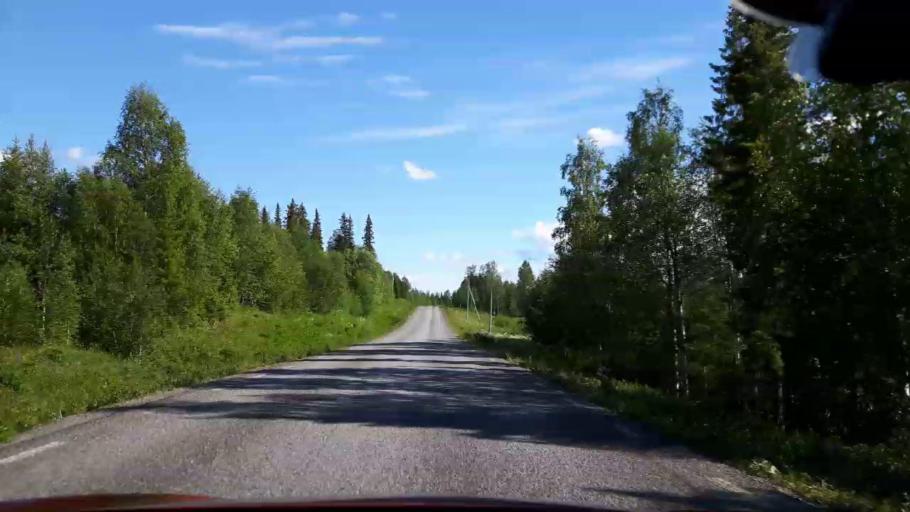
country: SE
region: Jaemtland
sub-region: Krokoms Kommun
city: Valla
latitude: 63.7186
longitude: 14.1313
